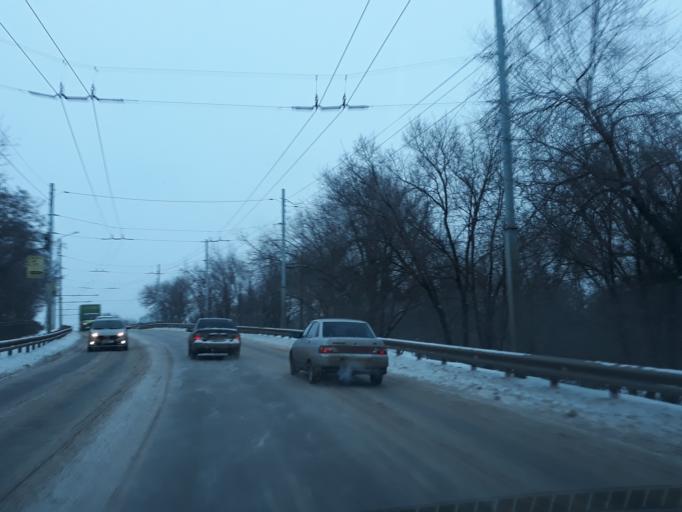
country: RU
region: Rostov
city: Taganrog
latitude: 47.2641
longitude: 38.9259
